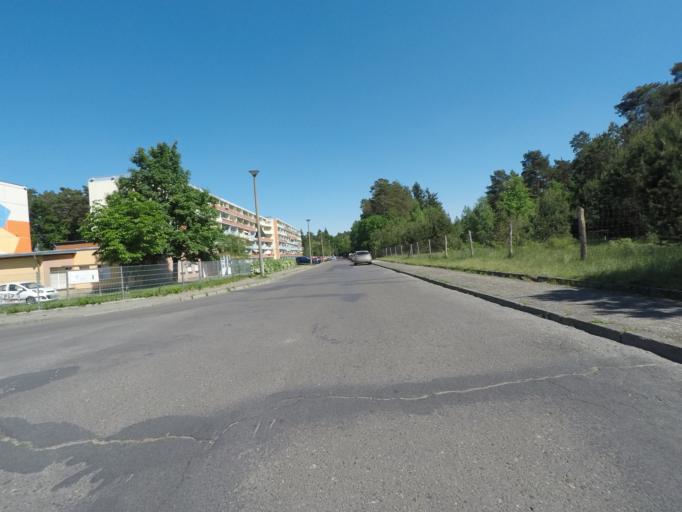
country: DE
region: Brandenburg
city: Eberswalde
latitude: 52.8281
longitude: 13.7644
